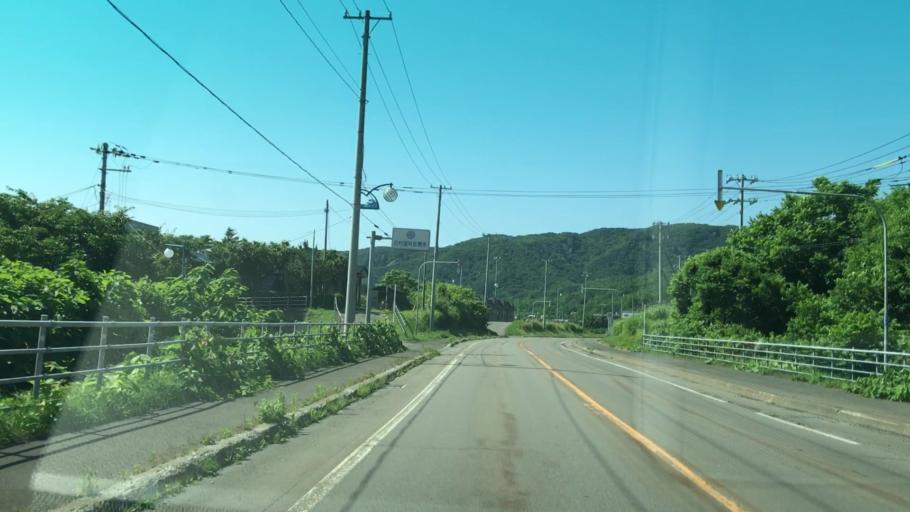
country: JP
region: Hokkaido
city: Iwanai
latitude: 43.0712
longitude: 140.4904
